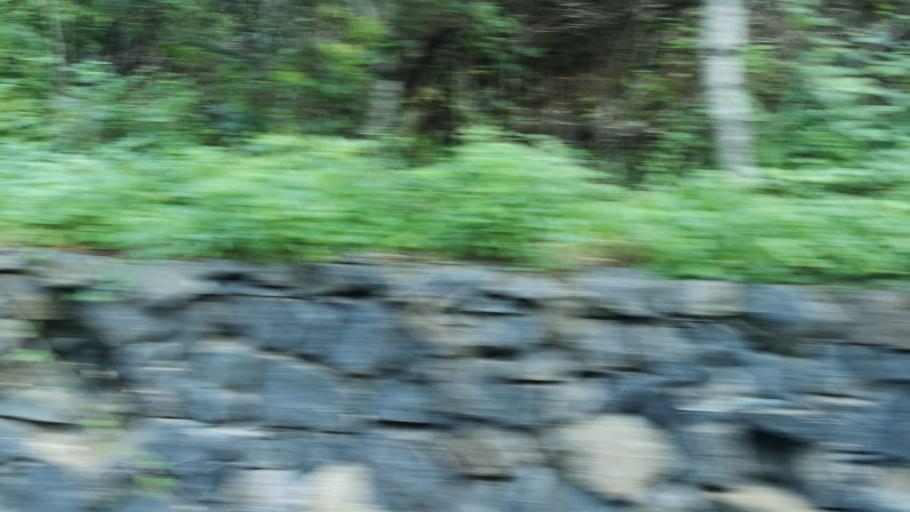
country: ES
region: Canary Islands
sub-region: Provincia de Santa Cruz de Tenerife
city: Hermigua
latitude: 28.1338
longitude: -17.1993
